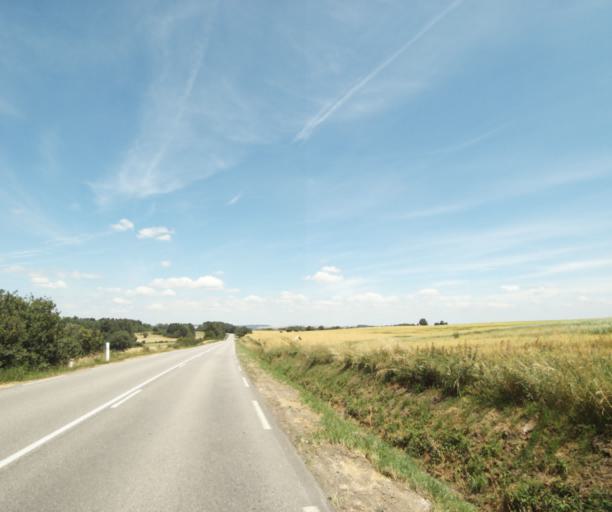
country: FR
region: Lorraine
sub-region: Departement de Meurthe-et-Moselle
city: Luneville
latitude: 48.6228
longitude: 6.4873
